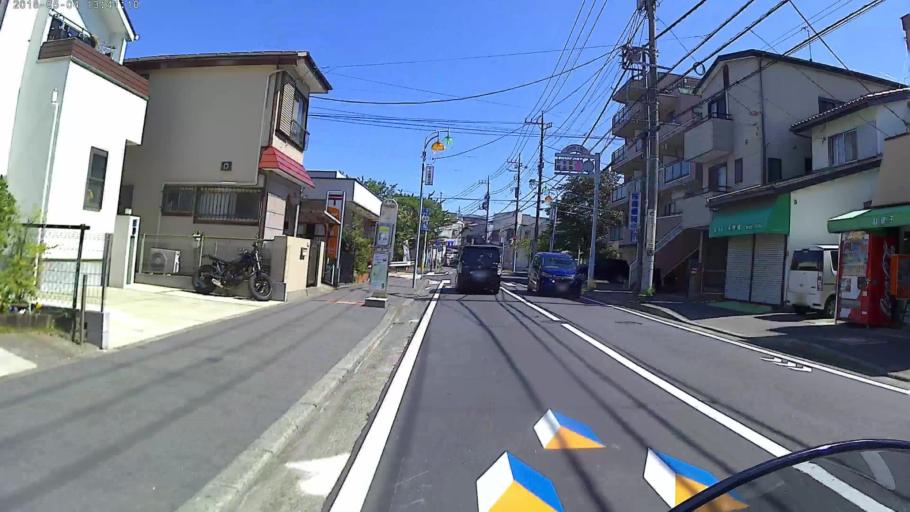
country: JP
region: Kanagawa
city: Minami-rinkan
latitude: 35.4387
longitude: 139.4587
